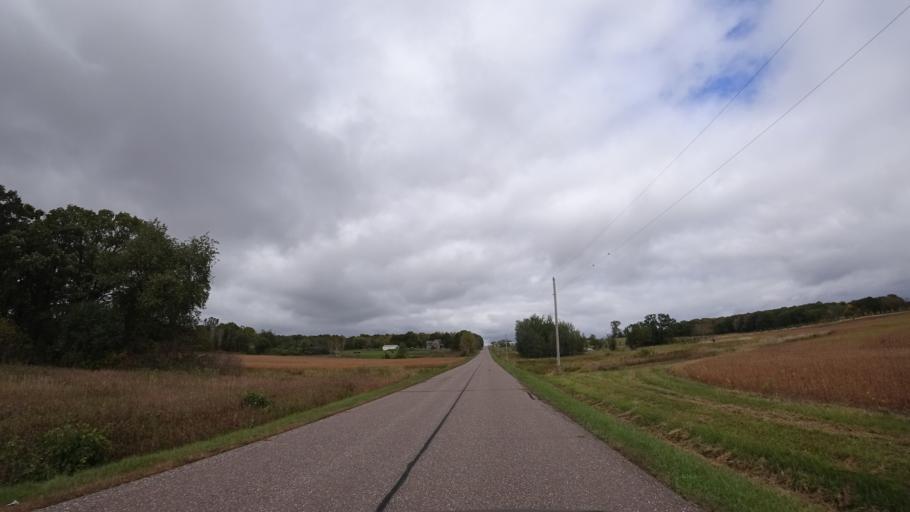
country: US
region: Wisconsin
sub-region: Chippewa County
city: Lake Wissota
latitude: 44.9861
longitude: -91.2868
